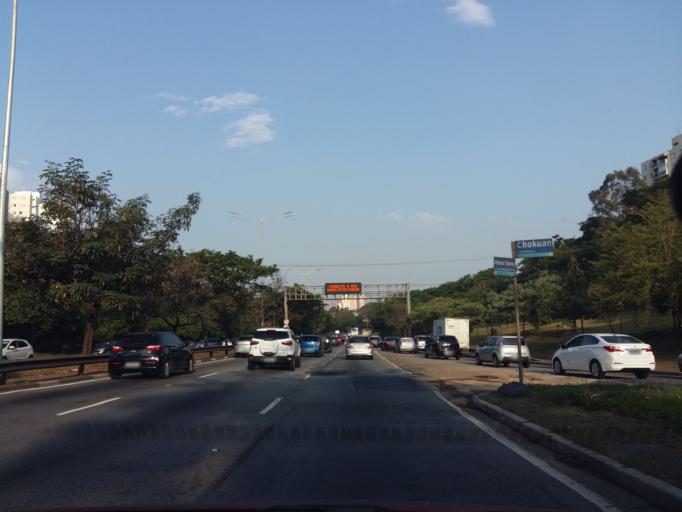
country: BR
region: Sao Paulo
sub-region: Diadema
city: Diadema
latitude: -23.6297
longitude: -46.6373
